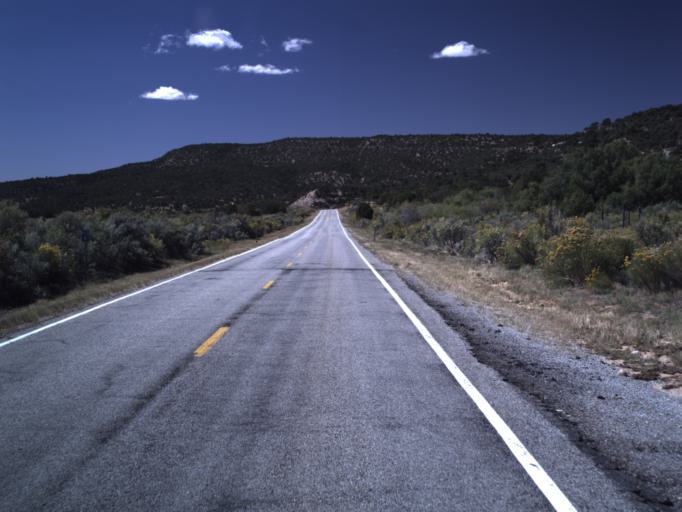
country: US
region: Utah
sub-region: Grand County
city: Moab
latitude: 38.3188
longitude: -109.3373
